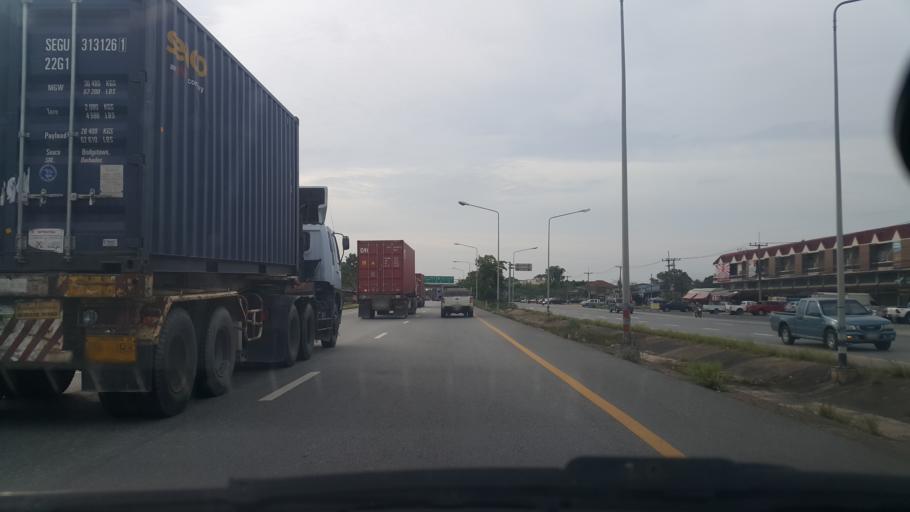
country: TH
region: Chon Buri
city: Bang Lamung
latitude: 12.9957
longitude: 100.9359
